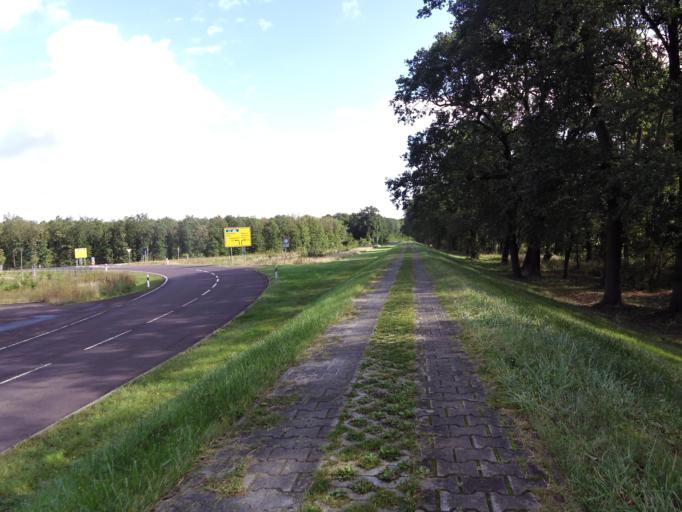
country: DE
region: Saxony-Anhalt
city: Schonebeck
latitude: 52.0277
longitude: 11.7621
